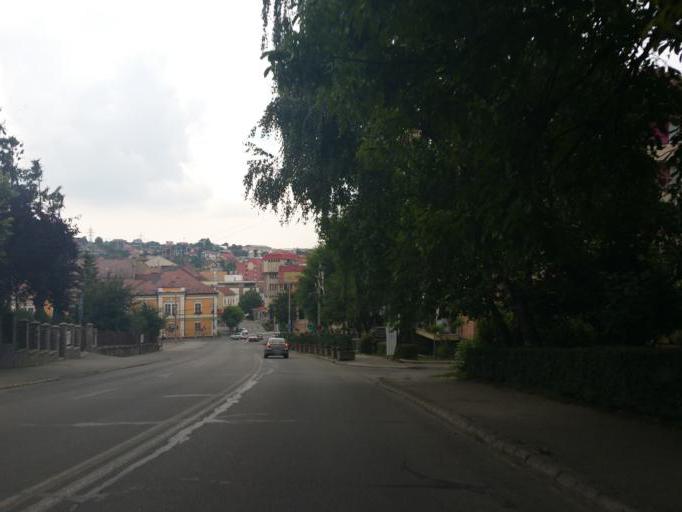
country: RO
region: Salaj
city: Zalau
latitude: 47.1770
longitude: 23.0570
